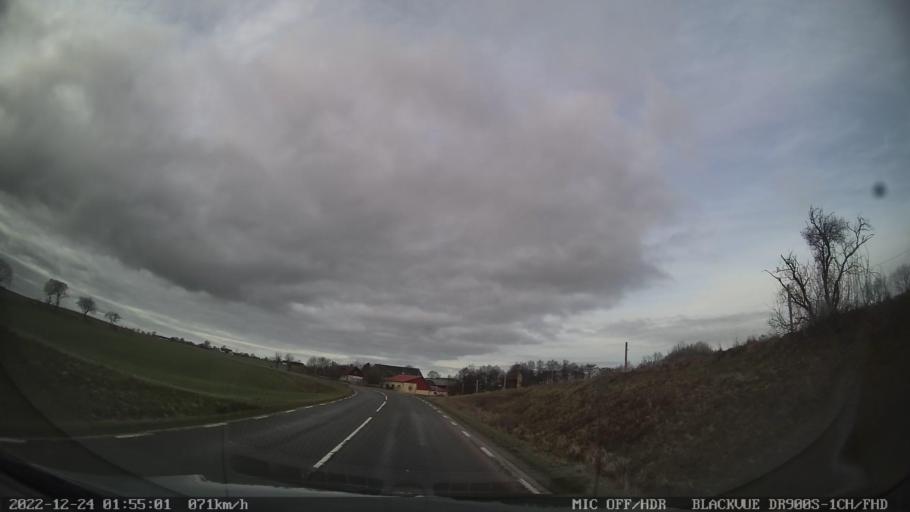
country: SE
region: Skane
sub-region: Tomelilla Kommun
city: Tomelilla
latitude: 55.5989
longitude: 14.0837
